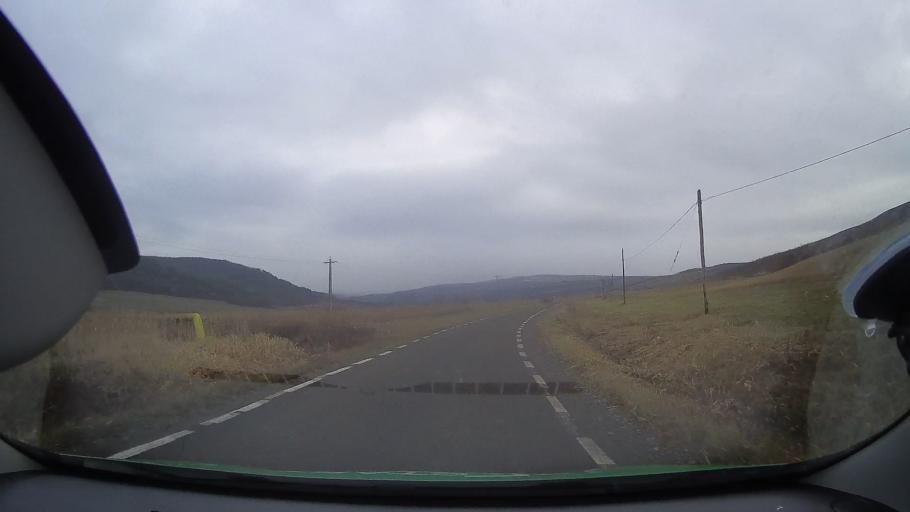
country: RO
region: Mures
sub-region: Comuna Bichis
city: Bichis
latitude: 46.3924
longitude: 24.0900
